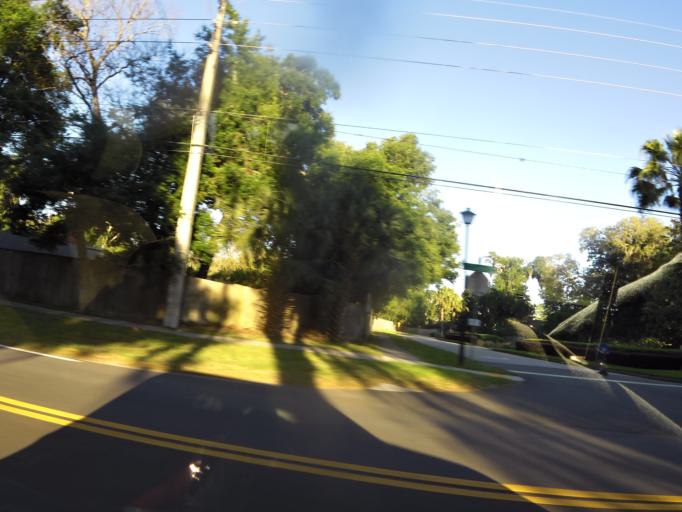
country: US
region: Florida
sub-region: Duval County
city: Atlantic Beach
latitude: 30.3724
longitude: -81.5135
